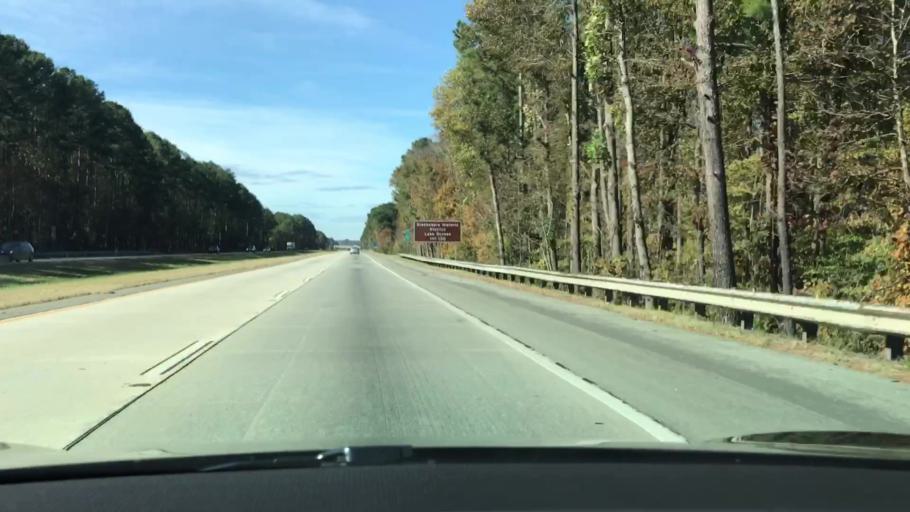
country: US
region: Georgia
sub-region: Greene County
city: Greensboro
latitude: 33.5471
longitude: -83.1840
